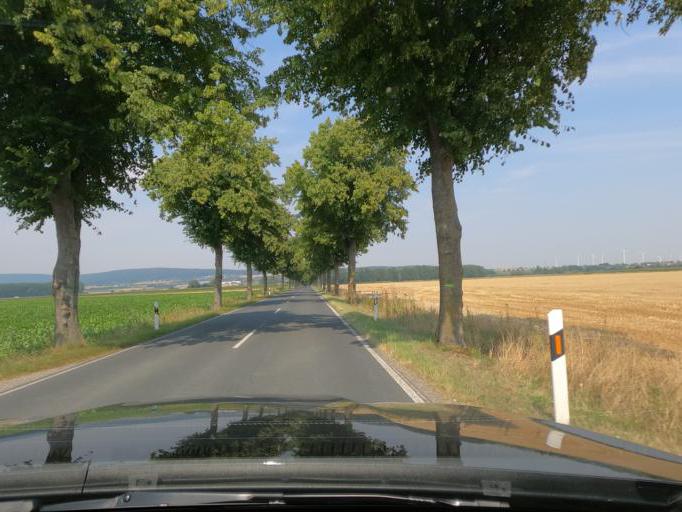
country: DE
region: Lower Saxony
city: Springe
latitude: 52.1863
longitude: 9.6382
